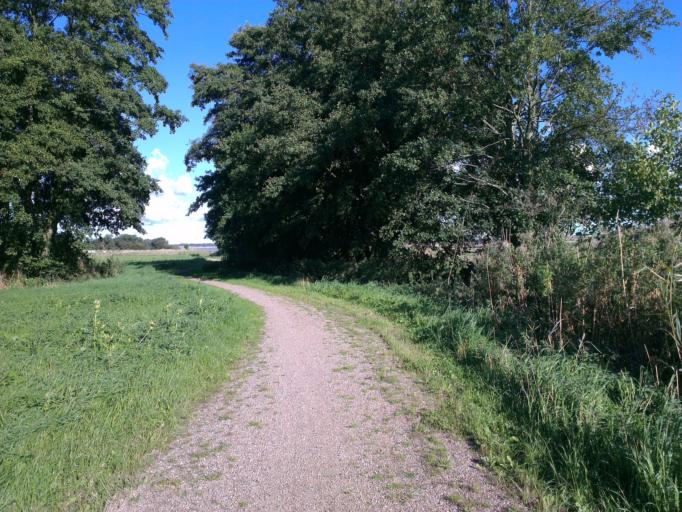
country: DK
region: Capital Region
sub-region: Frederikssund Kommune
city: Frederikssund
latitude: 55.8017
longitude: 12.0323
